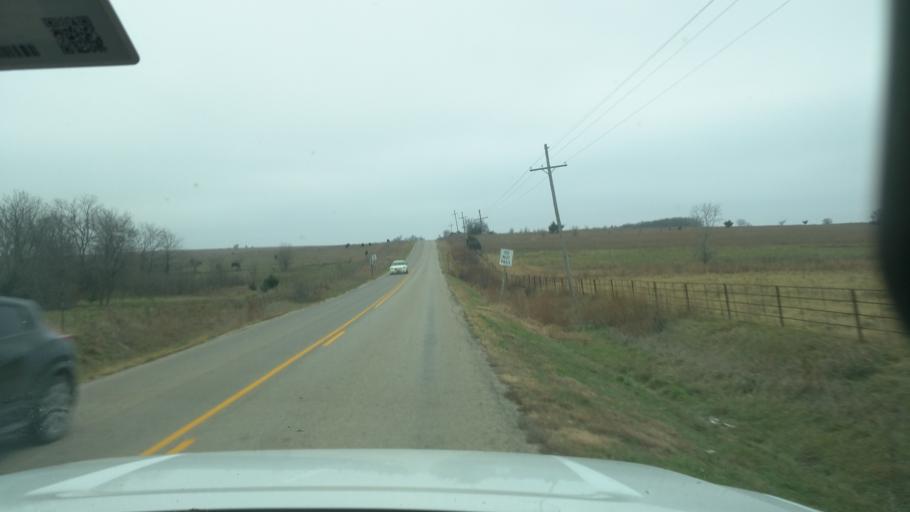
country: US
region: Kansas
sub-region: Lyon County
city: Emporia
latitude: 38.5880
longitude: -96.2610
